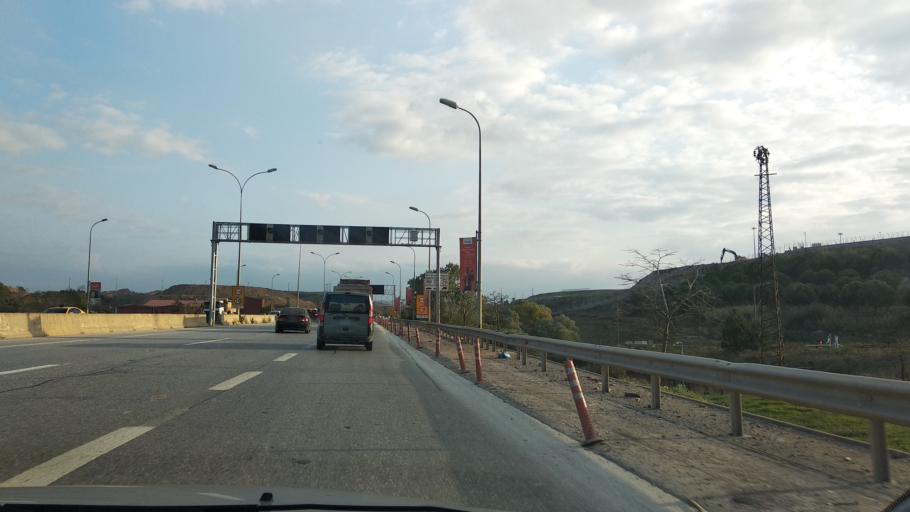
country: TR
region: Istanbul
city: Pendik
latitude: 40.9105
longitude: 29.3265
